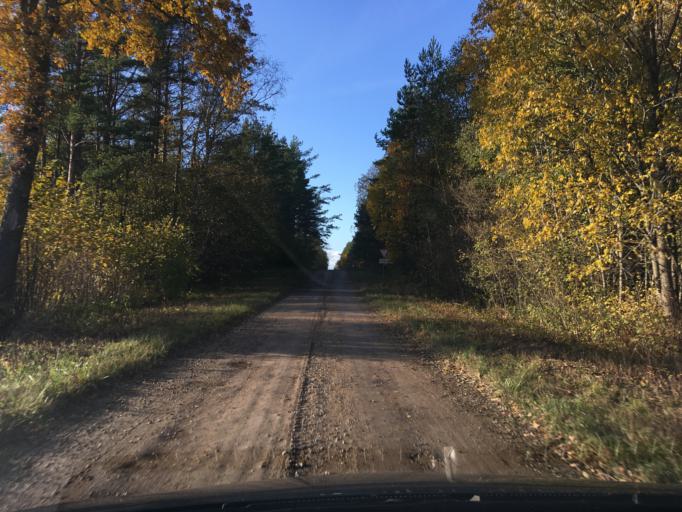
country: EE
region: Laeaene
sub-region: Lihula vald
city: Lihula
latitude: 58.5688
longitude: 23.7532
